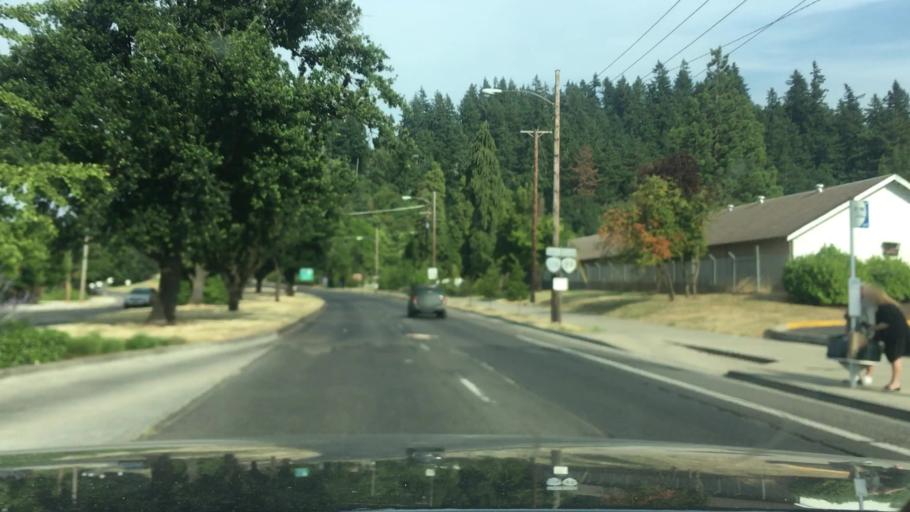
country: US
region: Oregon
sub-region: Lane County
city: Eugene
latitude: 44.0447
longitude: -123.0612
